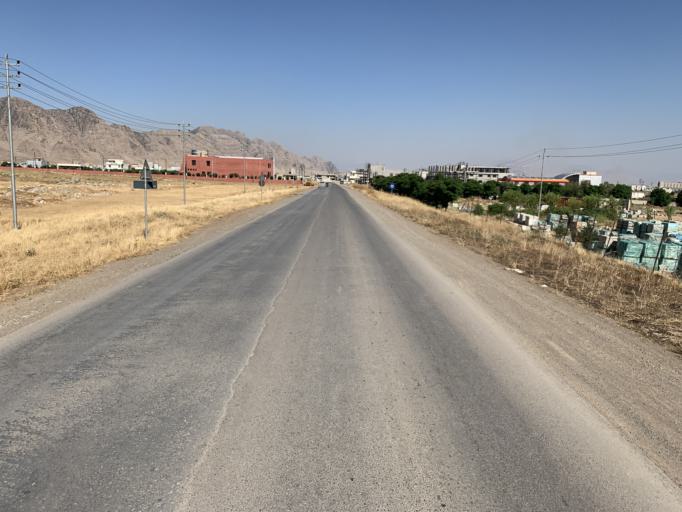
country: IQ
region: As Sulaymaniyah
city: Raniye
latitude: 36.2619
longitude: 44.8530
